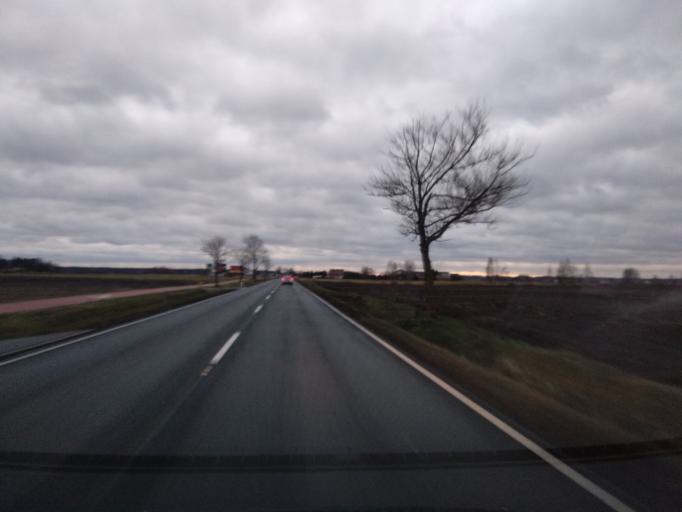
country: PL
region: Greater Poland Voivodeship
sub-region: Powiat koninski
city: Rychwal
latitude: 52.1097
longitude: 18.1674
